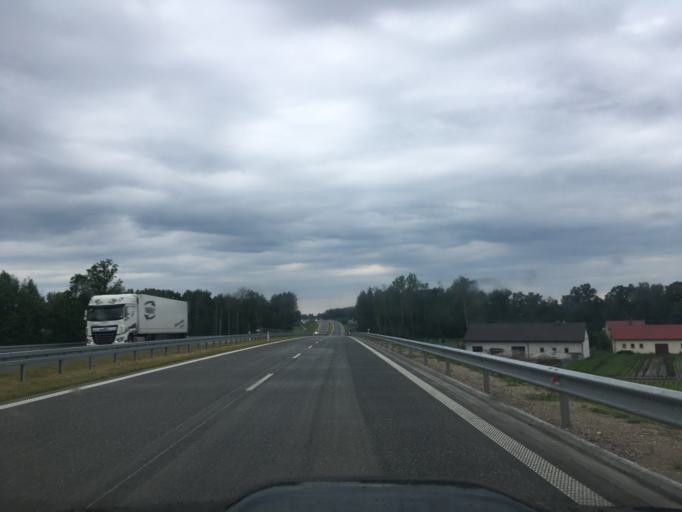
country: PL
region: Masovian Voivodeship
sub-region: Powiat piaseczynski
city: Baniocha
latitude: 51.9871
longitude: 21.1725
